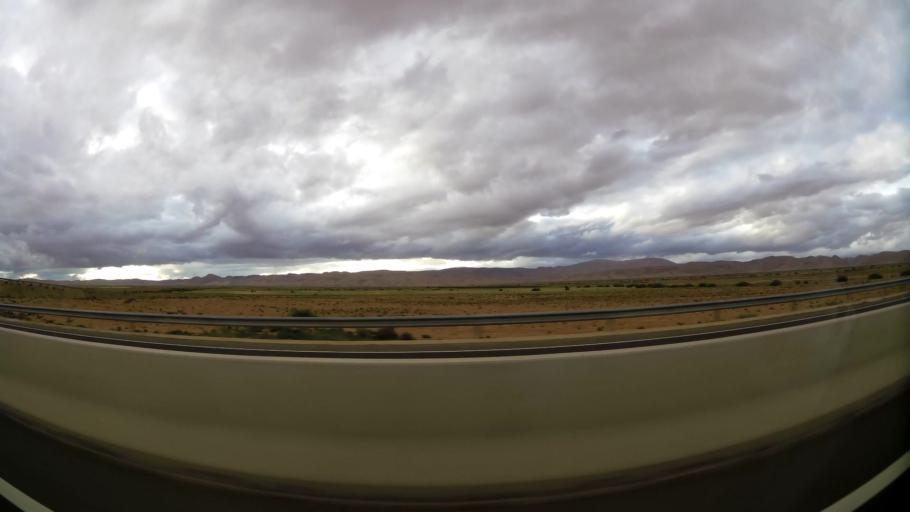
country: MA
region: Taza-Al Hoceima-Taounate
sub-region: Taza
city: Guercif
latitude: 34.3111
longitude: -3.6034
